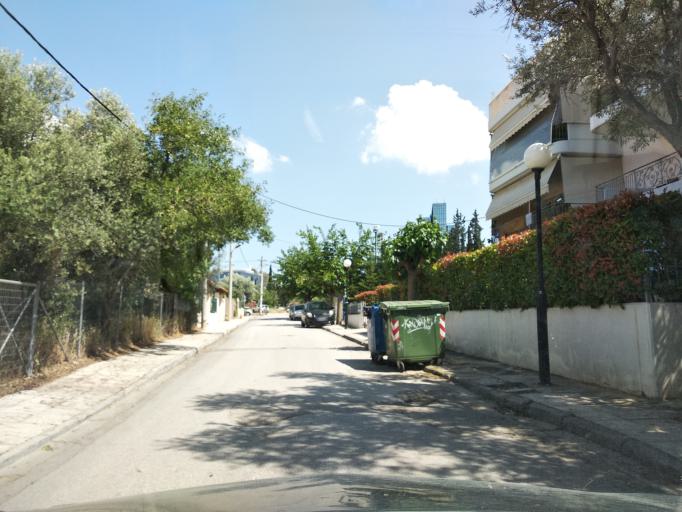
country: GR
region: Attica
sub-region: Nomarchia Athinas
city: Marousi
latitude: 38.0394
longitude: 23.7985
